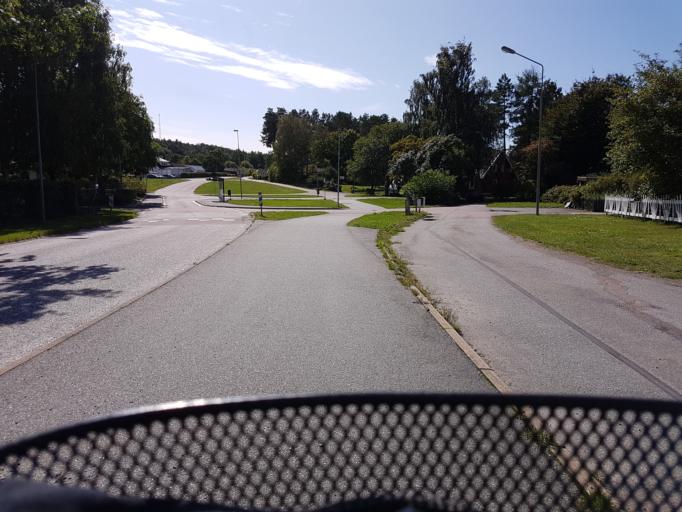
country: SE
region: Vaestra Goetaland
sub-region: Ale Kommun
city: Alvangen
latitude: 57.9483
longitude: 12.1081
